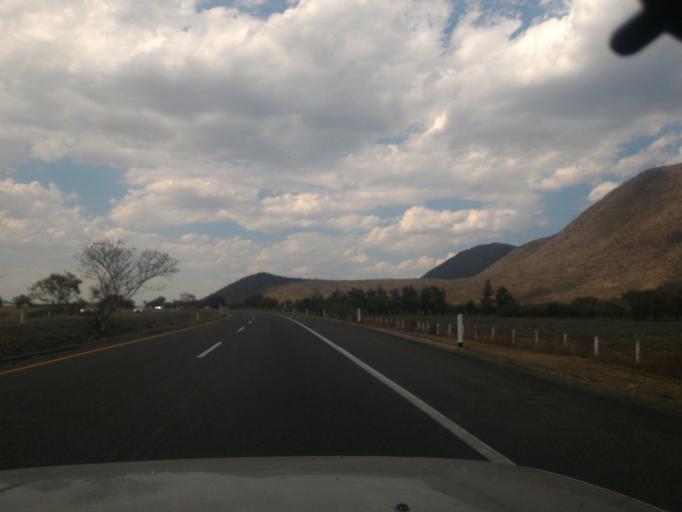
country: MX
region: Jalisco
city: Zacoalco de Torres
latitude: 20.1812
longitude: -103.5120
